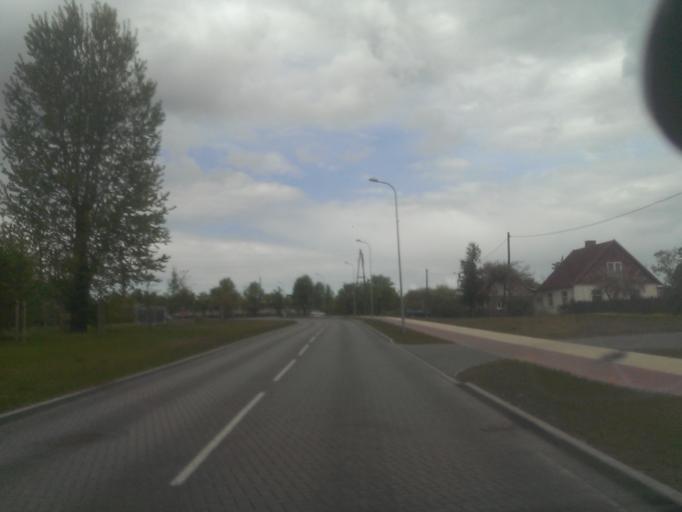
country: LV
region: Kuldigas Rajons
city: Kuldiga
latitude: 56.9787
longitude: 21.9504
